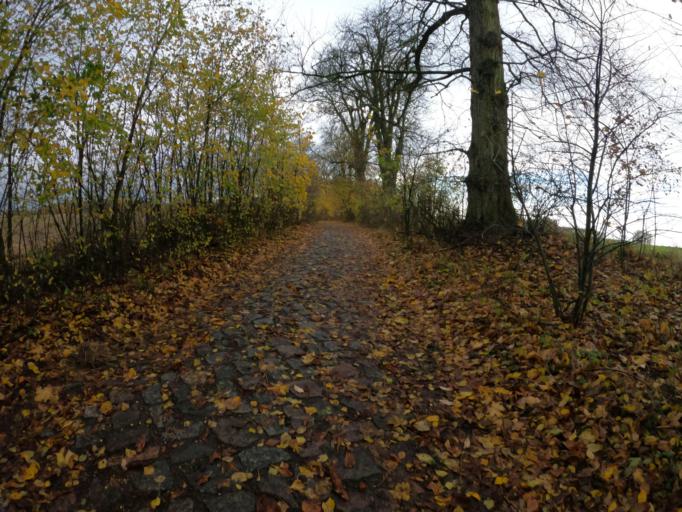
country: PL
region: West Pomeranian Voivodeship
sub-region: Powiat walecki
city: Tuczno
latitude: 53.2055
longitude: 16.2084
